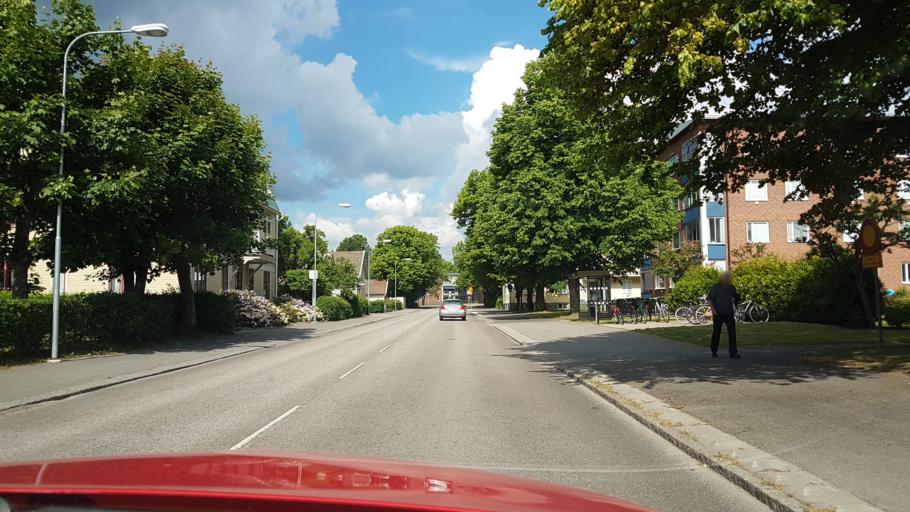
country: SE
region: Vaestra Goetaland
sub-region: Hjo Kommun
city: Hjo
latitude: 58.3056
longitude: 14.2889
